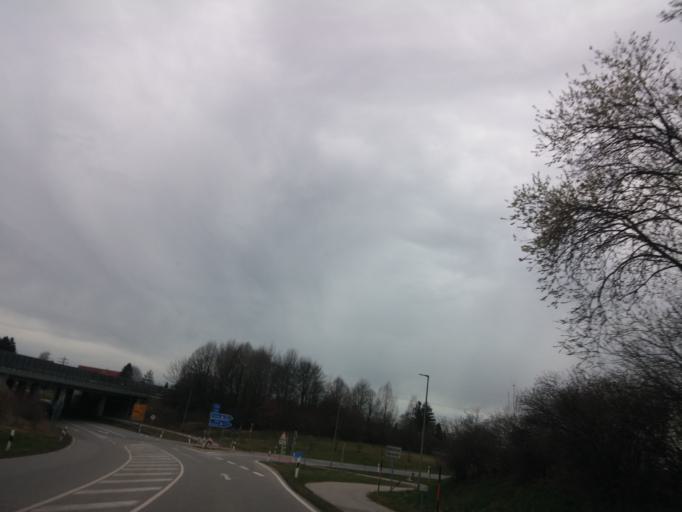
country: DE
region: Bavaria
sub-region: Swabia
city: Trunkelsberg
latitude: 47.9992
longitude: 10.2032
